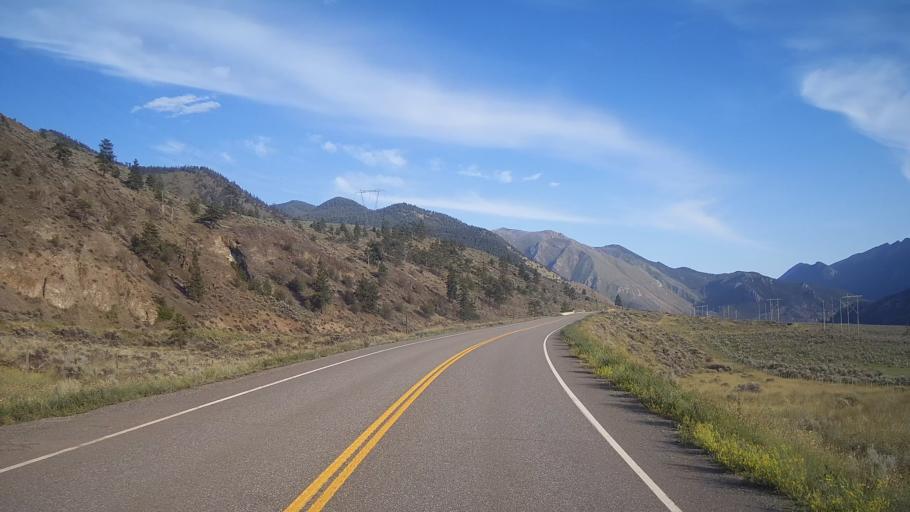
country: CA
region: British Columbia
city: Lillooet
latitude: 50.8151
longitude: -121.8520
